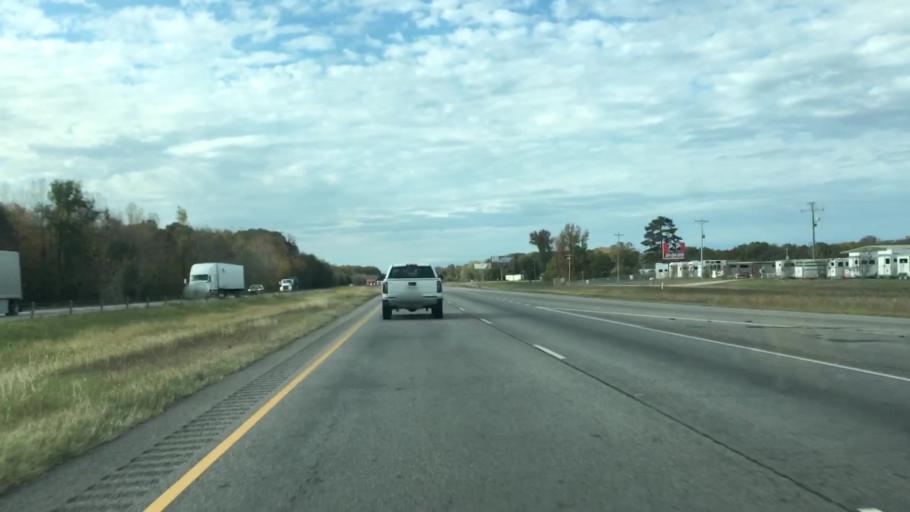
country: US
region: Arkansas
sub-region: Pope County
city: Atkins
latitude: 35.2215
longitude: -92.8328
